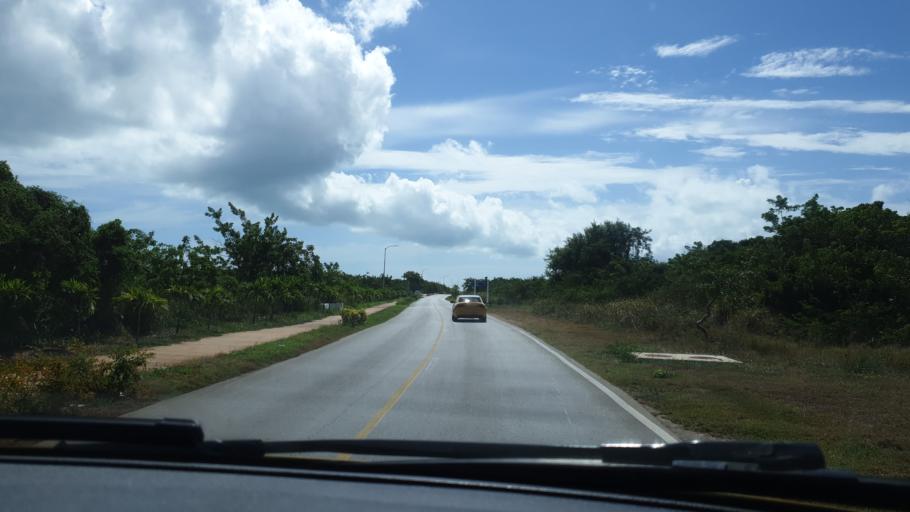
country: CU
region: Sancti Spiritus
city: Yaguajay
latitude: 22.6558
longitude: -79.0332
